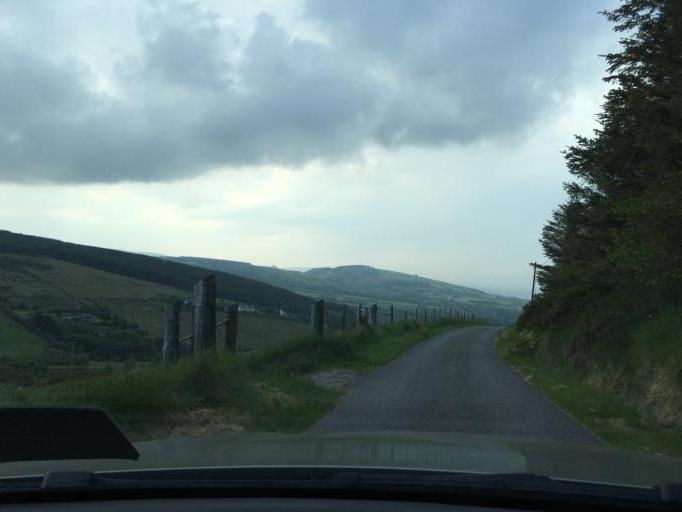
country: IE
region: Leinster
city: Ballinteer
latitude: 53.2481
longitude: -6.2703
